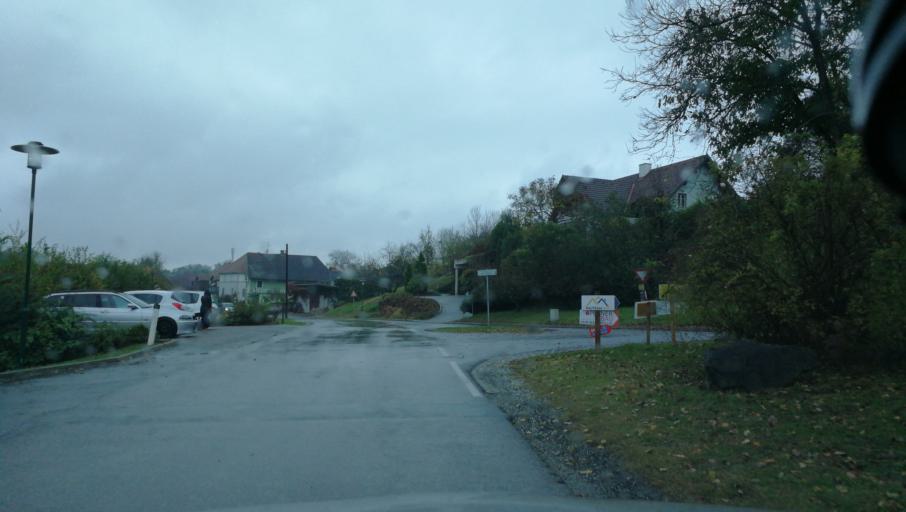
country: AT
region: Styria
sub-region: Politischer Bezirk Leibnitz
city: Sankt Veit am Vogau
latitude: 46.7478
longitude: 15.6286
